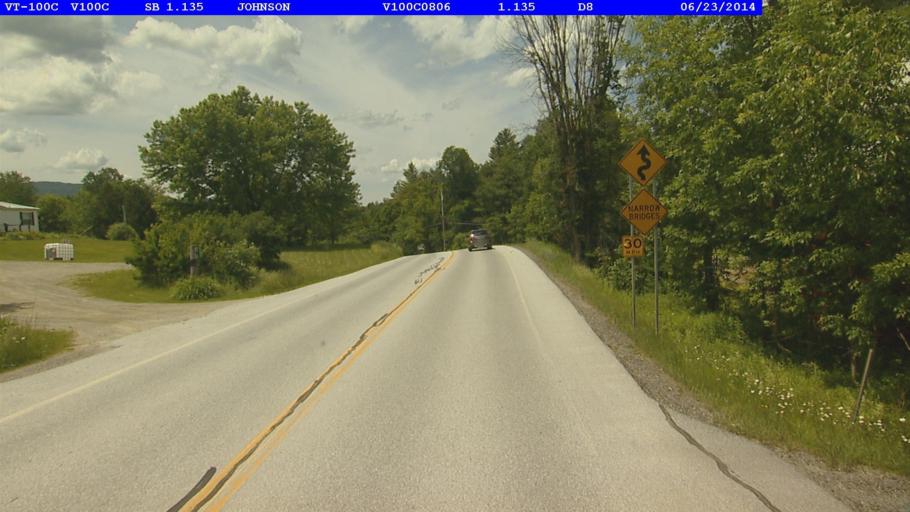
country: US
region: Vermont
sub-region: Lamoille County
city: Johnson
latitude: 44.6402
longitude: -72.6575
